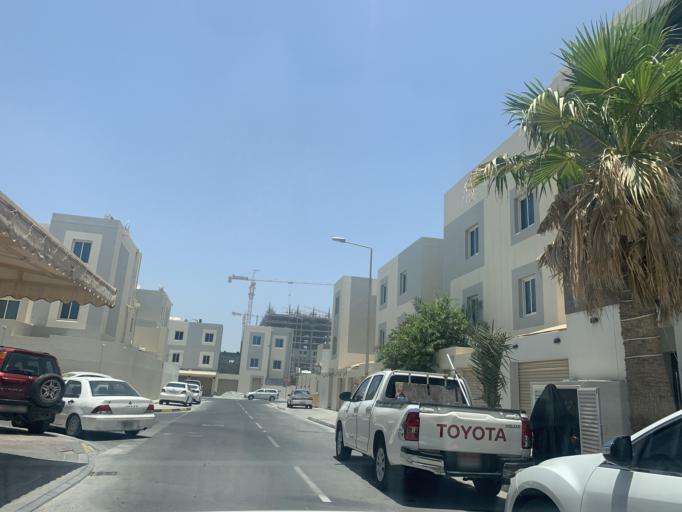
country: BH
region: Manama
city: Jidd Hafs
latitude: 26.2354
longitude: 50.4586
